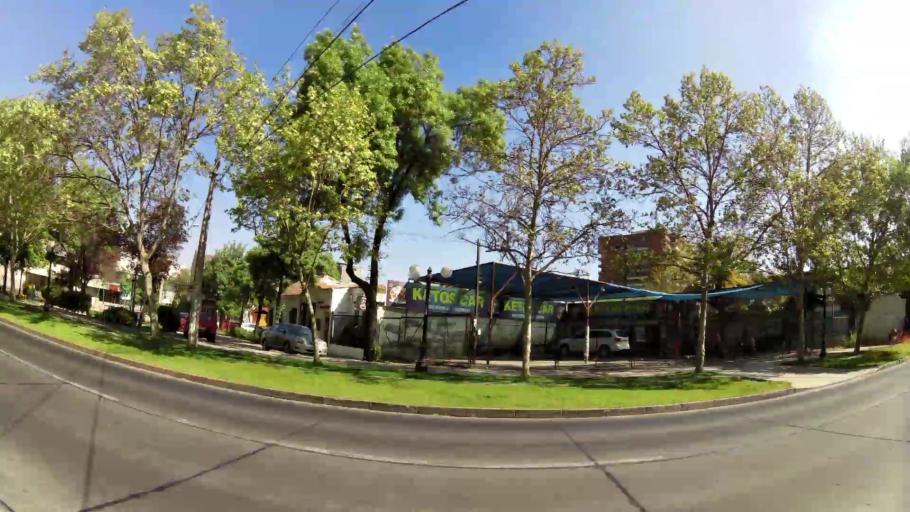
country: CL
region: Santiago Metropolitan
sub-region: Provincia de Santiago
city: Santiago
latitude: -33.4451
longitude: -70.6182
